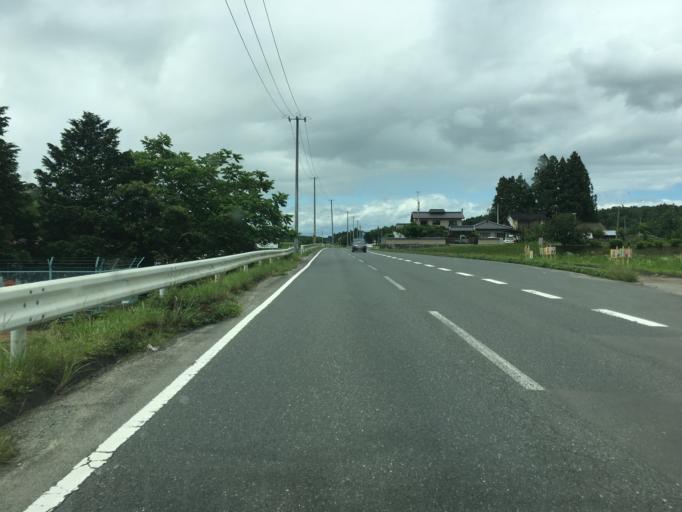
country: JP
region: Miyagi
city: Marumori
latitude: 37.7294
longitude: 140.9291
